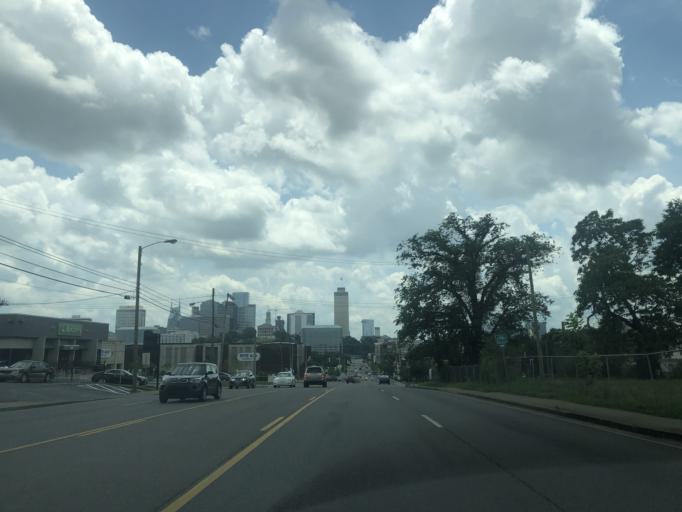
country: US
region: Tennessee
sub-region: Davidson County
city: Nashville
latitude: 36.1746
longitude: -86.7923
